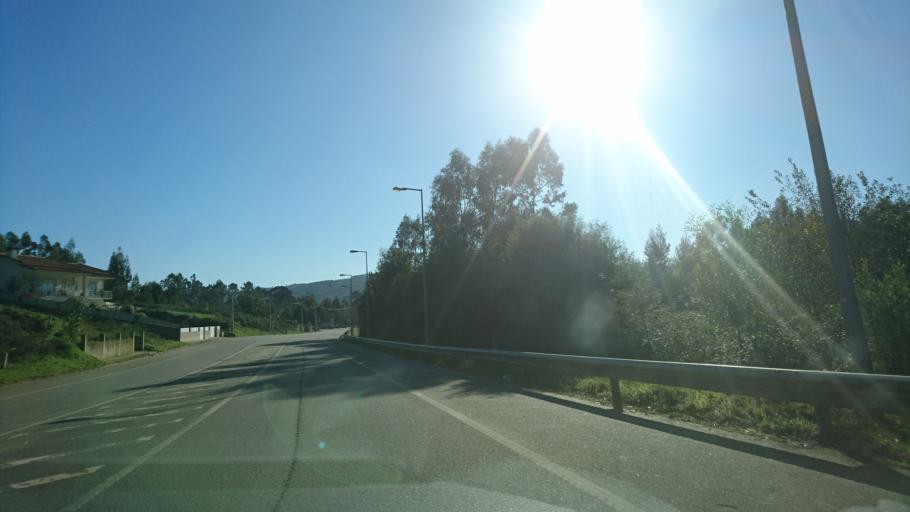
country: PT
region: Porto
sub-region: Paredes
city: Recarei
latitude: 41.1509
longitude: -8.3948
